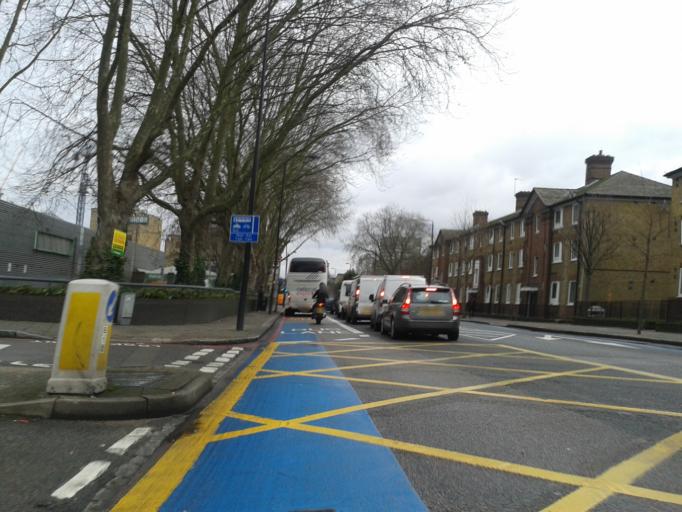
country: GB
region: England
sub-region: Greater London
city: Earlsfield
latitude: 51.4658
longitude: -0.1797
